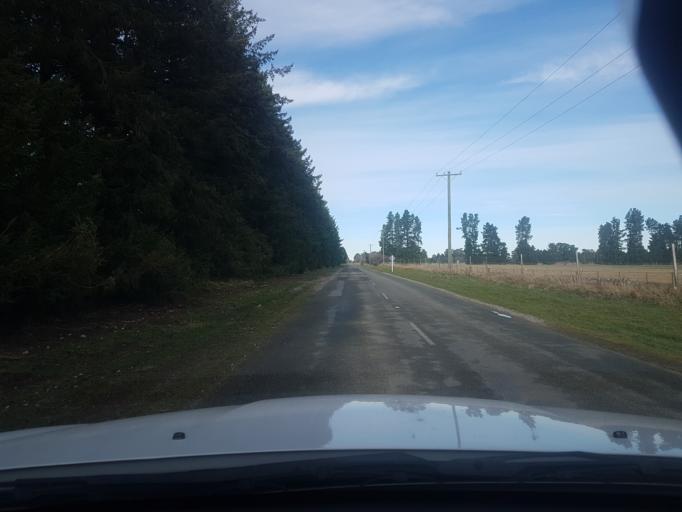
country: NZ
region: Canterbury
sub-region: Timaru District
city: Pleasant Point
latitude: -43.9585
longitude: 171.2652
